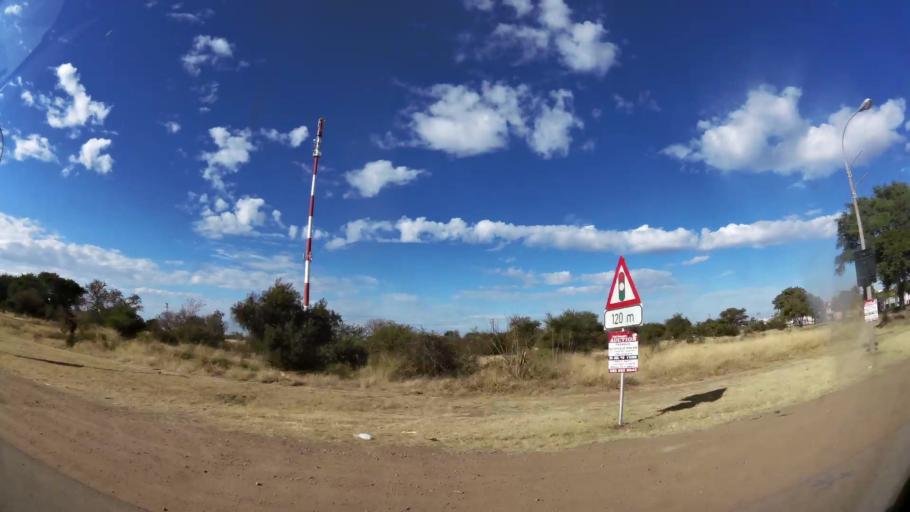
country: ZA
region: Limpopo
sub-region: Waterberg District Municipality
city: Bela-Bela
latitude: -24.8917
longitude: 28.2964
